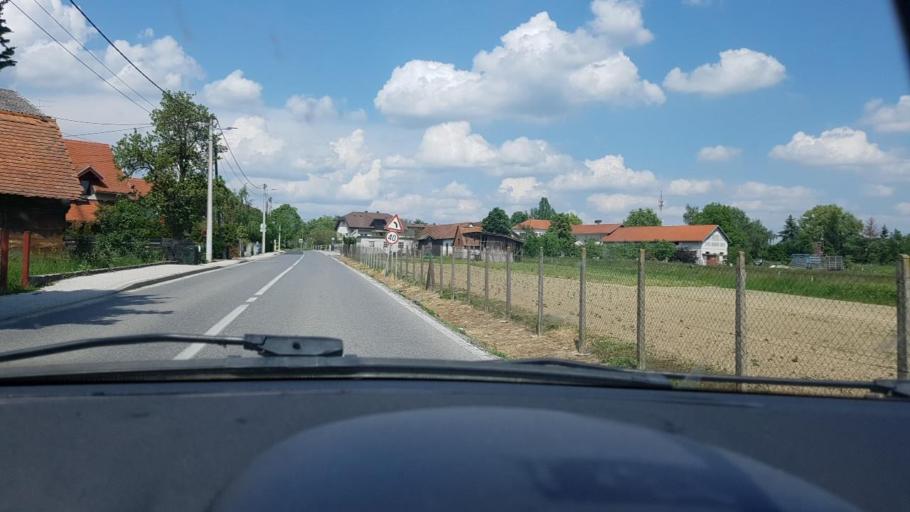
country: HR
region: Grad Zagreb
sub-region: Sesvete
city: Sesvete
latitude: 45.8854
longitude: 16.1739
